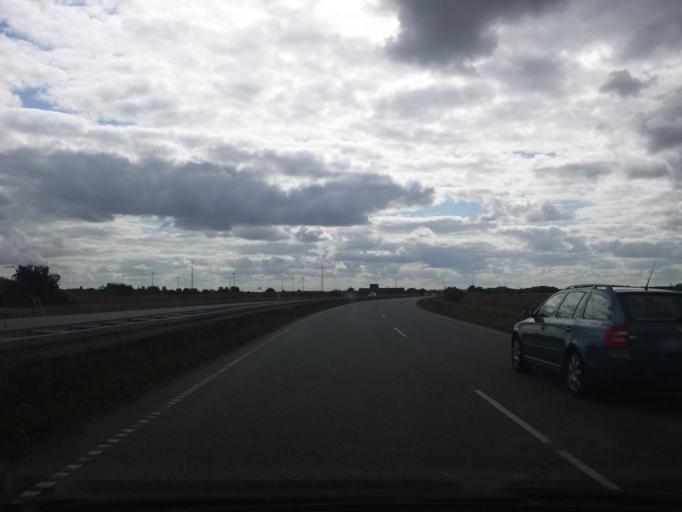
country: DK
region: South Denmark
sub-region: Sonderborg Kommune
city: Augustenborg
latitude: 54.9360
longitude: 9.8721
